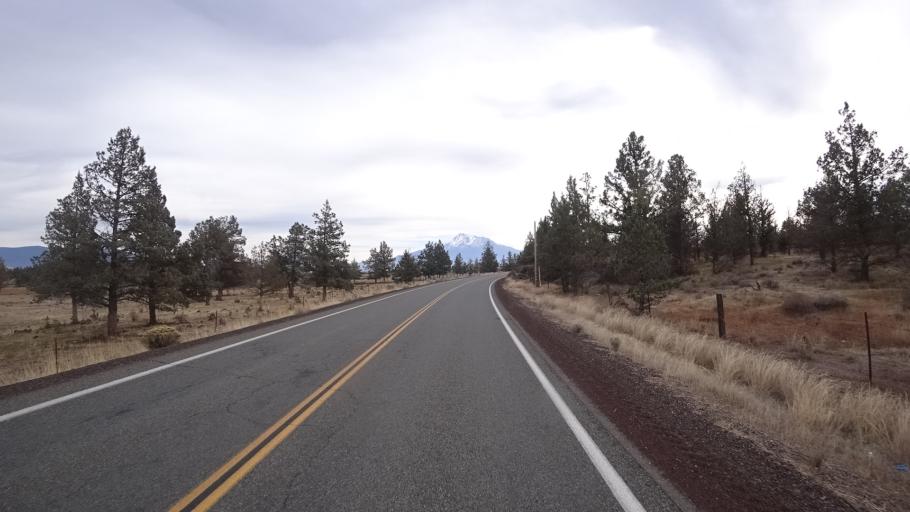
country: US
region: California
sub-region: Siskiyou County
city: Montague
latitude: 41.6332
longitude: -122.4355
